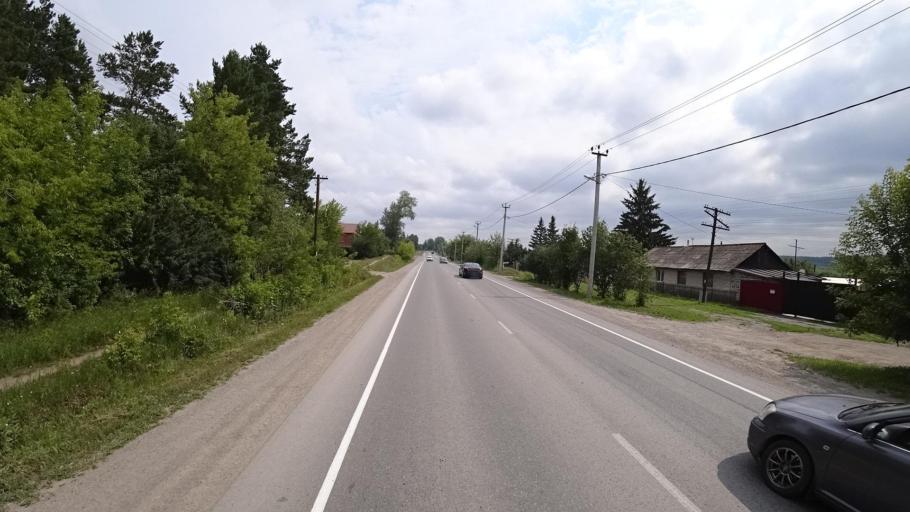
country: RU
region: Sverdlovsk
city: Obukhovskoye
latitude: 56.8458
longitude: 62.6517
